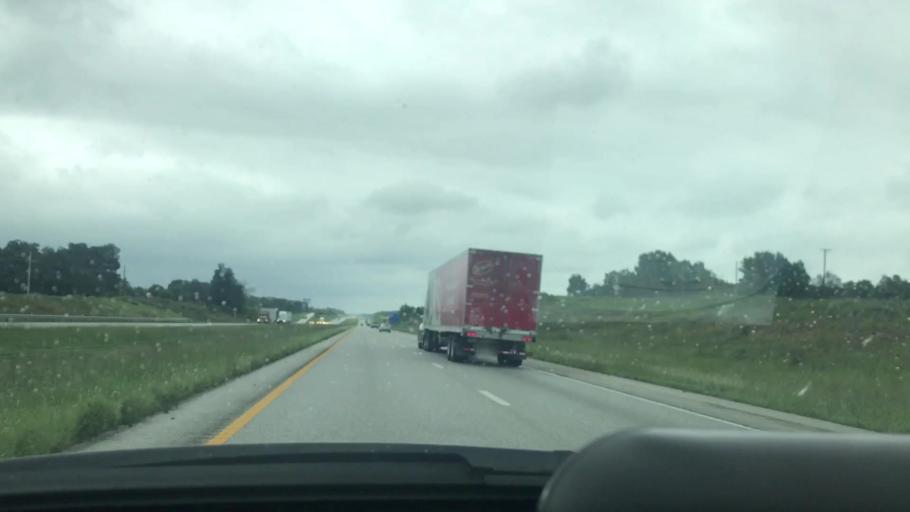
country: US
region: Missouri
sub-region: Jasper County
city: Duenweg
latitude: 37.0818
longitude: -94.3333
